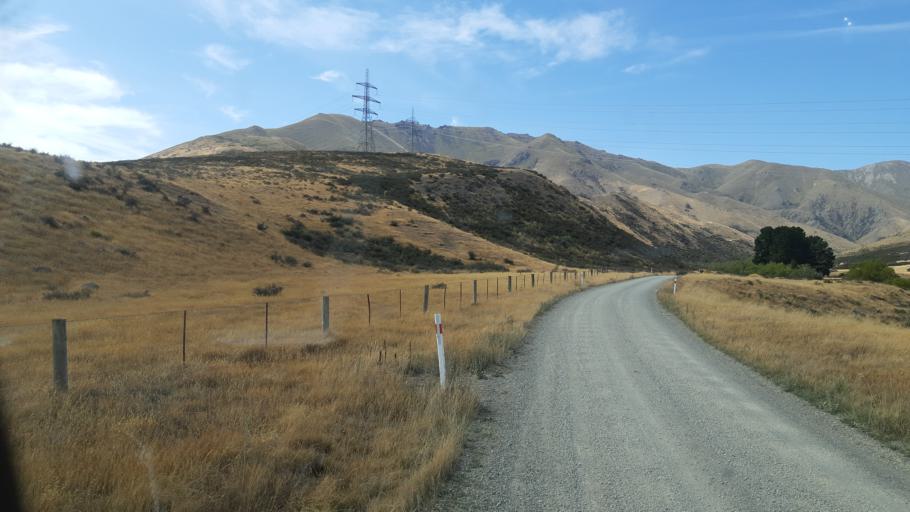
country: NZ
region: Canterbury
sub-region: Timaru District
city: Pleasant Point
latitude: -44.1958
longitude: 170.5828
